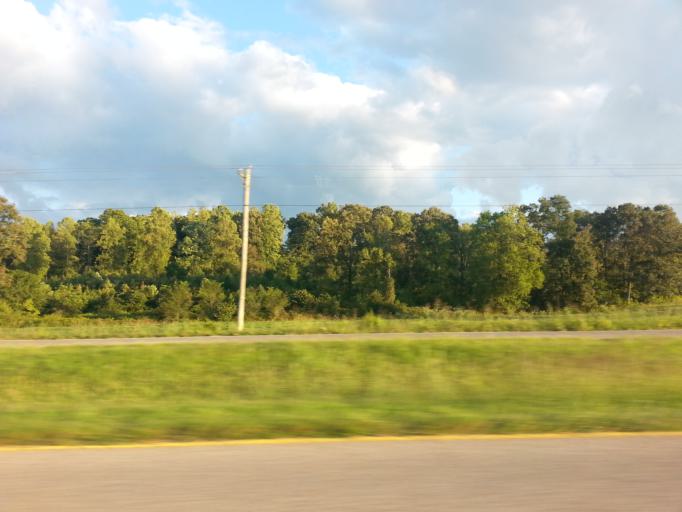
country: US
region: Tennessee
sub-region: Jefferson County
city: New Market
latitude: 36.0875
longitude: -83.5978
